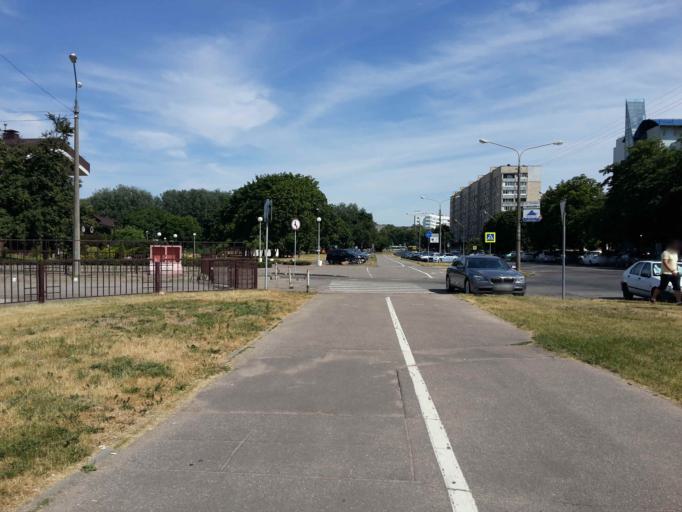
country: BY
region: Minsk
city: Minsk
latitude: 53.9279
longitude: 27.5670
